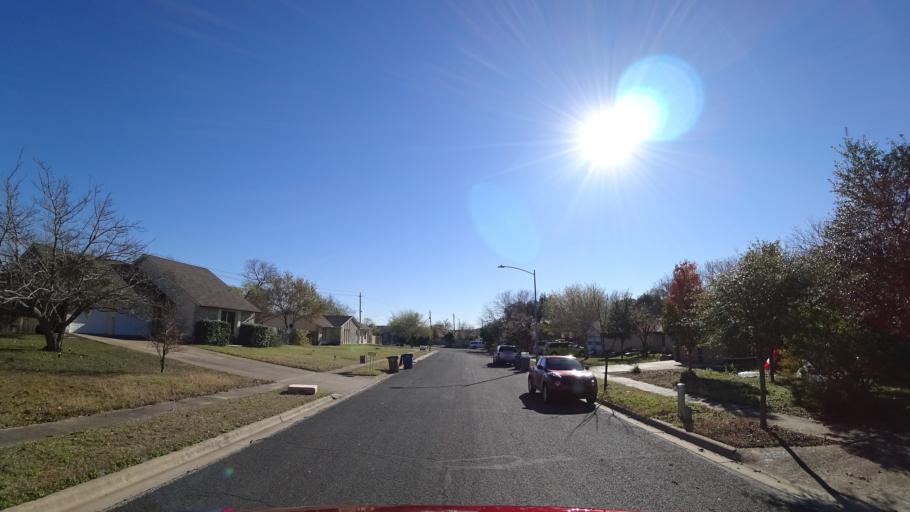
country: US
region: Texas
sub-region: Travis County
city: Wells Branch
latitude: 30.4176
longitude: -97.6943
